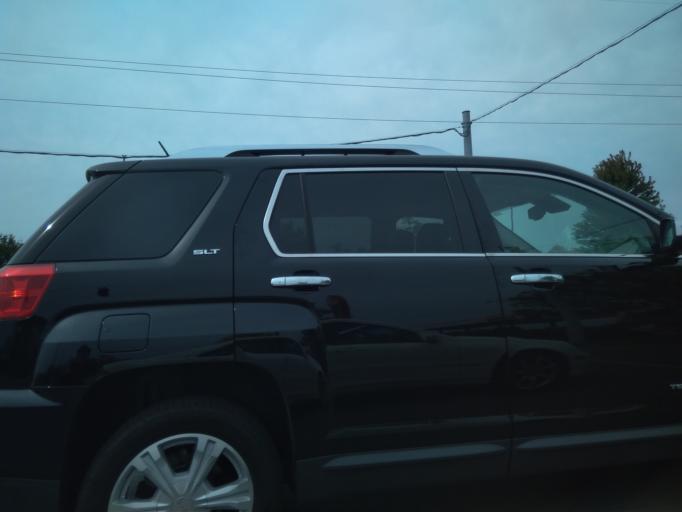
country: US
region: Kentucky
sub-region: Jefferson County
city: Worthington
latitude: 38.3070
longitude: -85.5753
